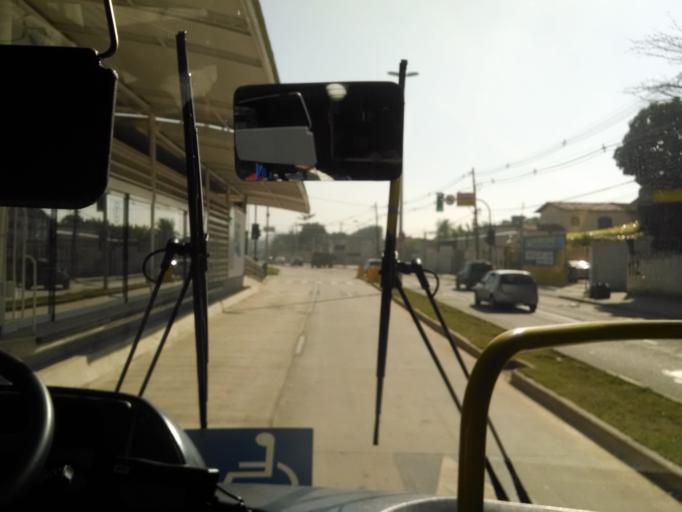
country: BR
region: Rio de Janeiro
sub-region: Nilopolis
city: Nilopolis
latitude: -22.9679
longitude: -43.3907
